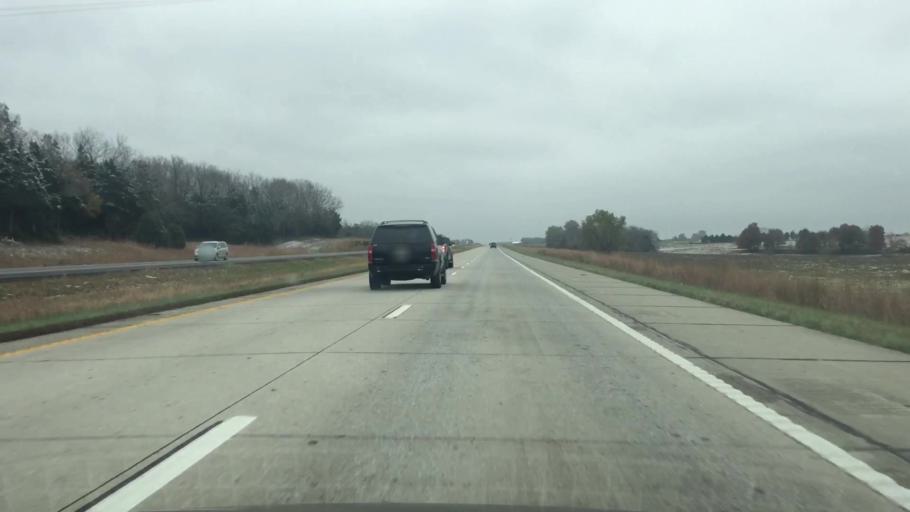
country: US
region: Missouri
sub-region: Saint Clair County
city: Osceola
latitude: 38.0045
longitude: -93.6566
